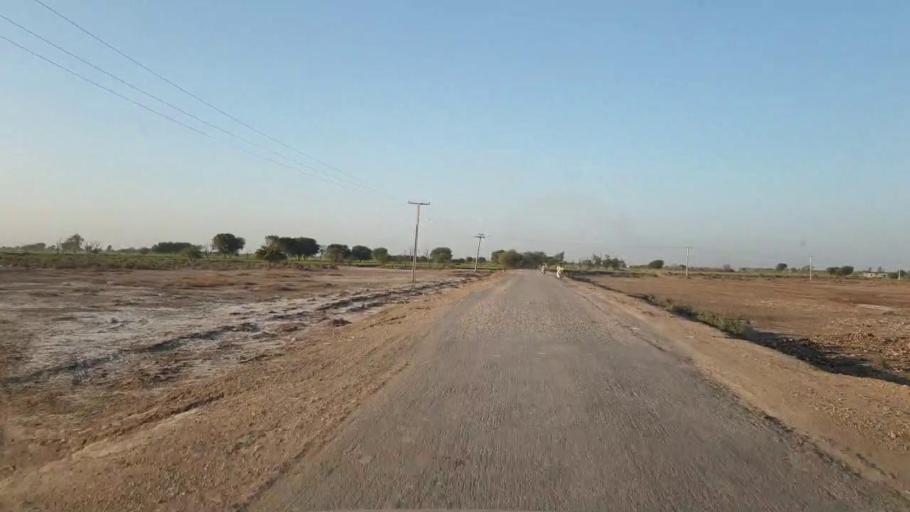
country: PK
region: Sindh
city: Tando Allahyar
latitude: 25.3751
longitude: 68.7480
